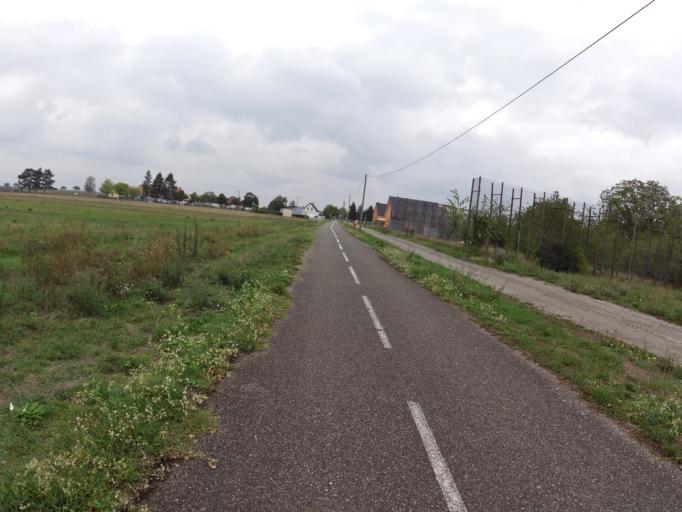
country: FR
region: Alsace
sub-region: Departement du Haut-Rhin
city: Fessenheim
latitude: 47.9242
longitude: 7.5337
